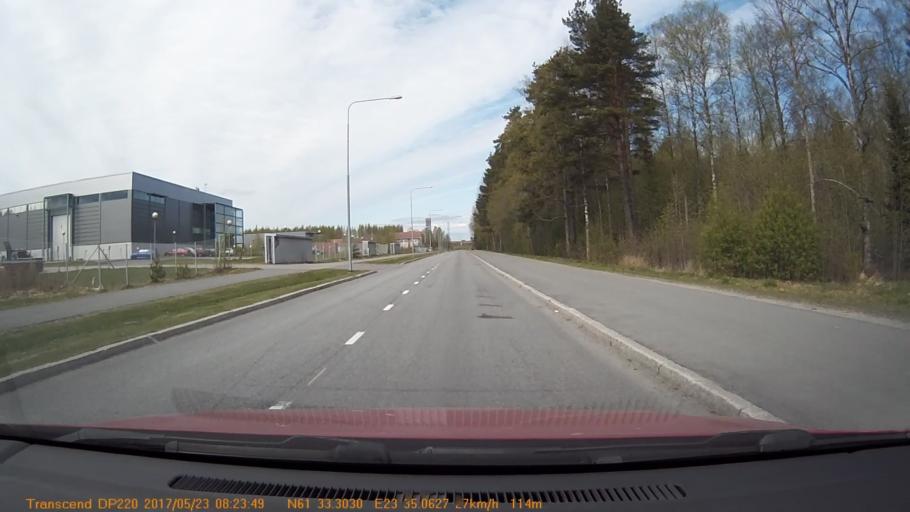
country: FI
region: Pirkanmaa
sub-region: Tampere
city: Yloejaervi
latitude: 61.5550
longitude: 23.5842
